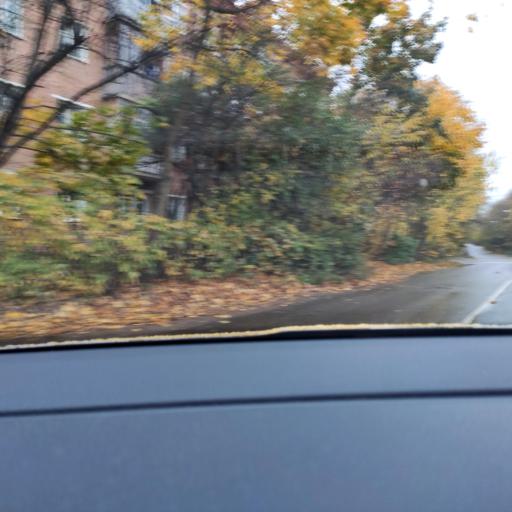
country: RU
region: Moskovskaya
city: Ivanteyevka
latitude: 55.9724
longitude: 37.8988
